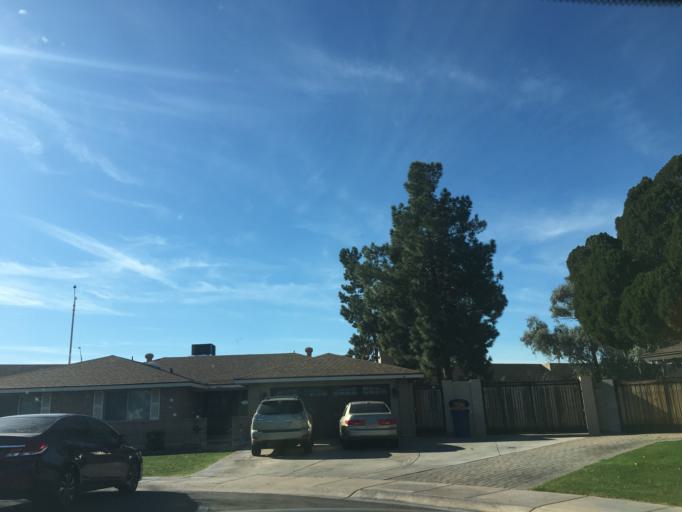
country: US
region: Arizona
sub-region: Maricopa County
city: Tempe
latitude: 33.3866
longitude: -111.9044
